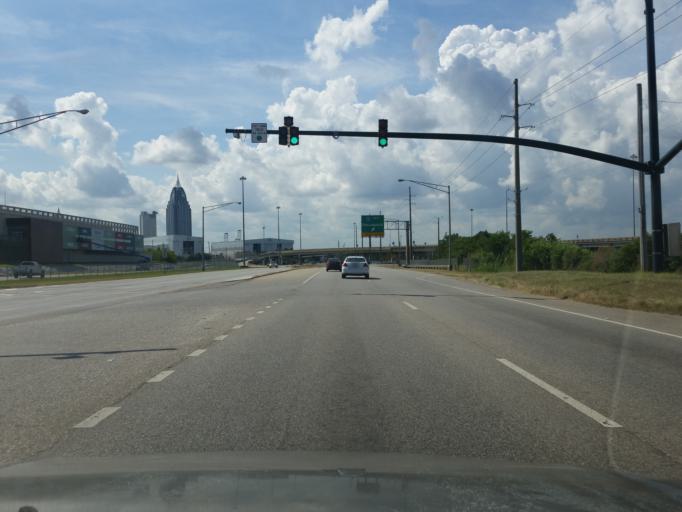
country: US
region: Alabama
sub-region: Mobile County
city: Mobile
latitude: 30.6897
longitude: -88.0218
